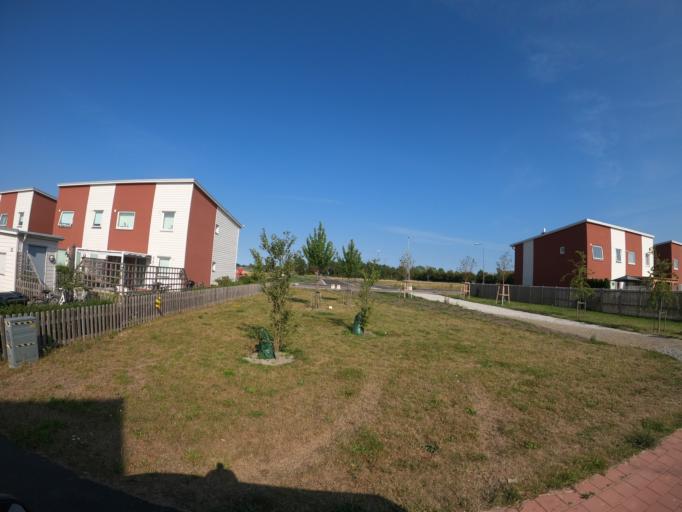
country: SE
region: Skane
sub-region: Lunds Kommun
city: Lund
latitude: 55.7510
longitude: 13.1898
